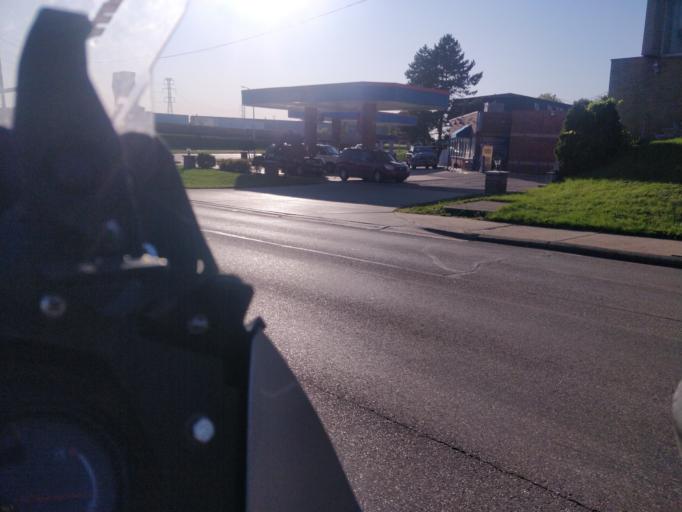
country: US
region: Michigan
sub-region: Wayne County
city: Melvindale
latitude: 42.2738
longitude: -83.1943
